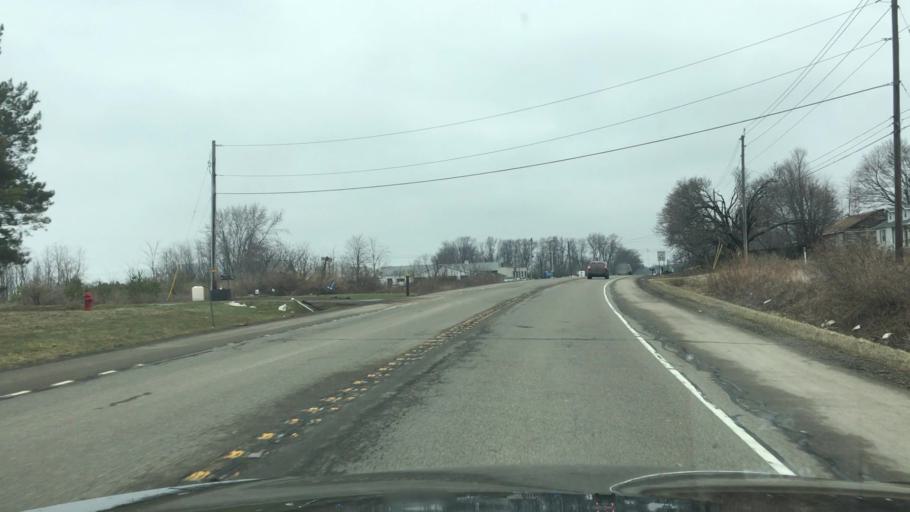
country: US
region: New York
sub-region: Chautauqua County
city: Fredonia
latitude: 42.4367
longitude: -79.3064
